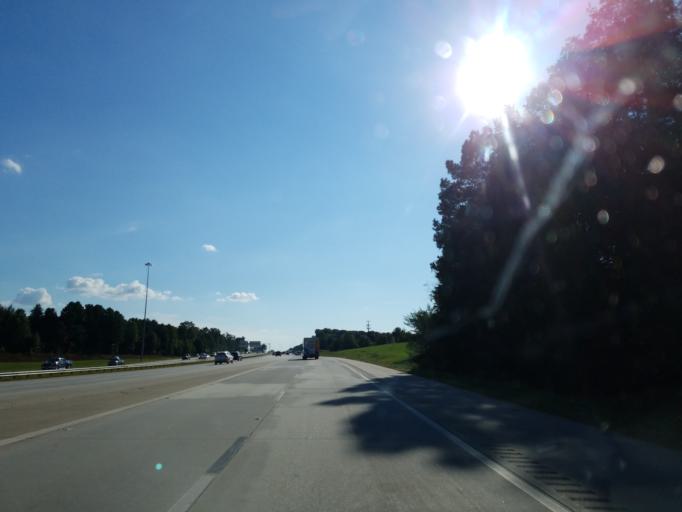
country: US
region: North Carolina
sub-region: Davidson County
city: Tyro
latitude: 35.7708
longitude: -80.3278
